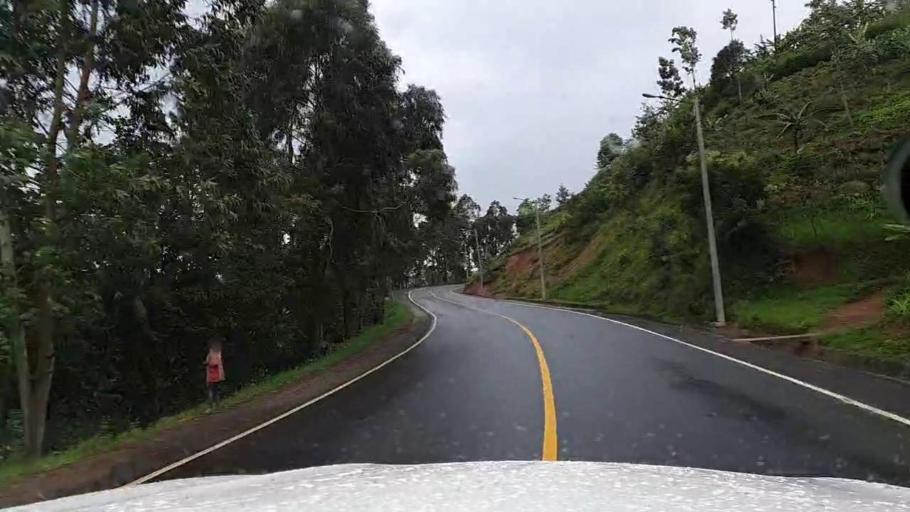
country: RW
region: Northern Province
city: Byumba
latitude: -1.6633
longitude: 29.8433
